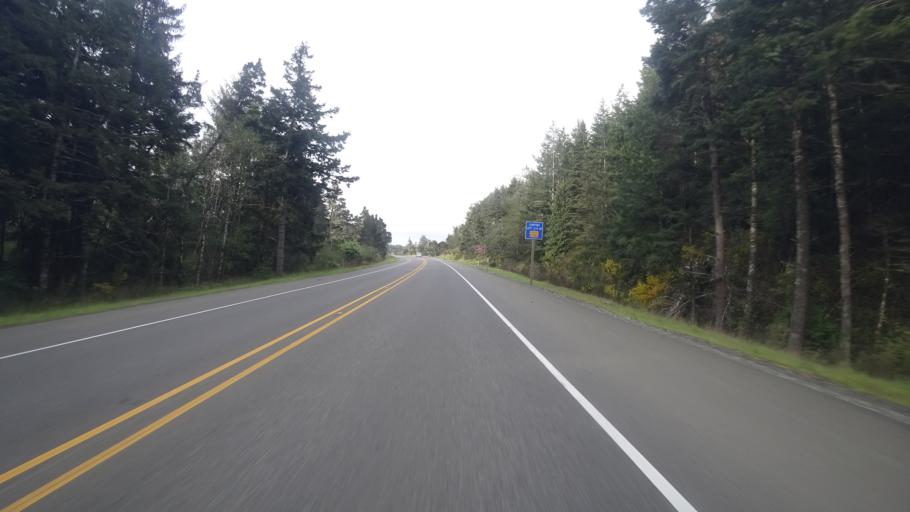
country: US
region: Oregon
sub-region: Coos County
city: Bandon
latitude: 43.1541
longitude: -124.3951
